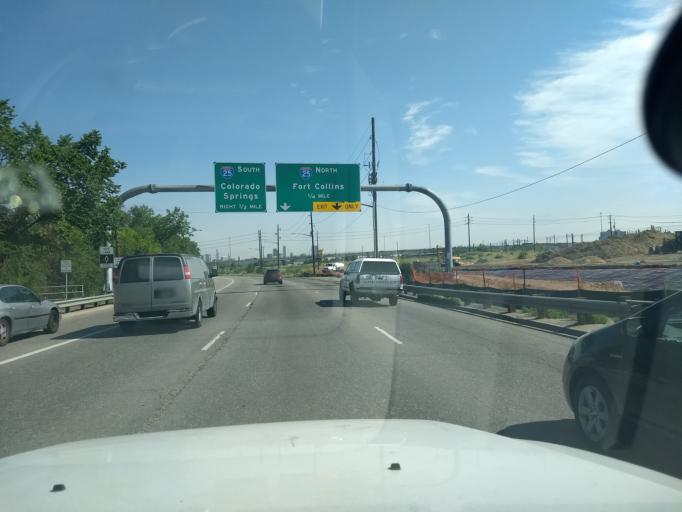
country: US
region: Colorado
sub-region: Denver County
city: Denver
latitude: 39.6973
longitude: -104.9918
